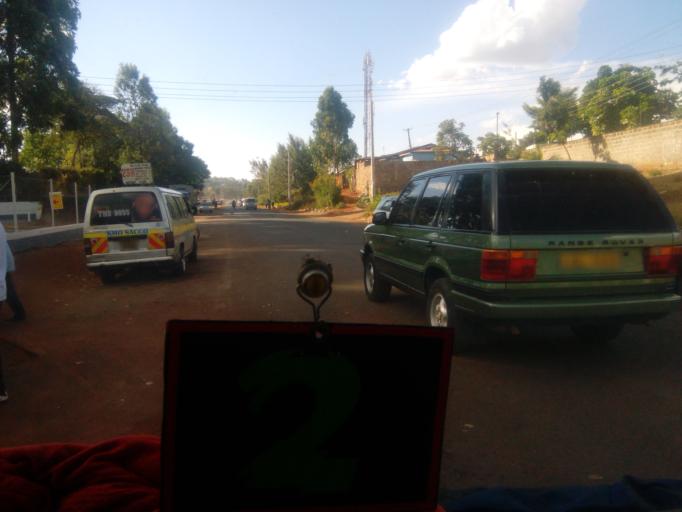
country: KE
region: Kiambu
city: Kikuyu
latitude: -1.2805
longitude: 36.6906
